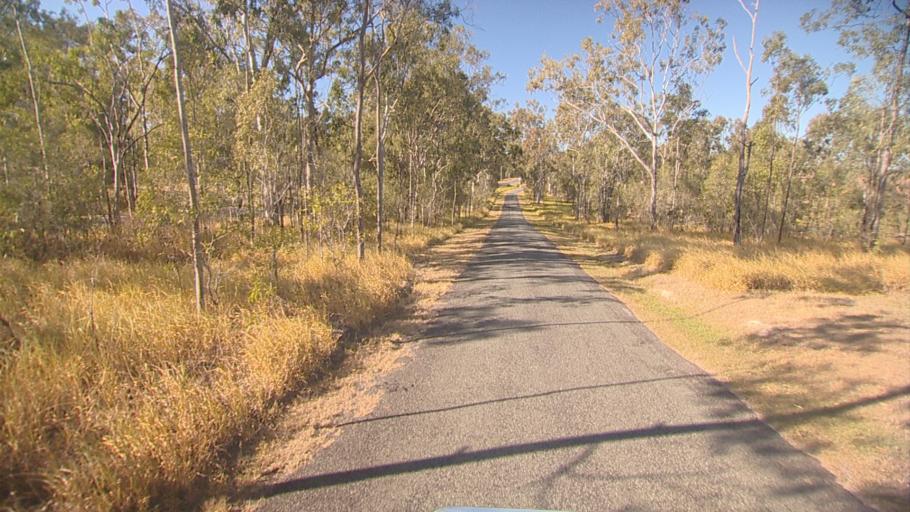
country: AU
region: Queensland
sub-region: Logan
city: North Maclean
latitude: -27.7974
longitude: 153.0204
